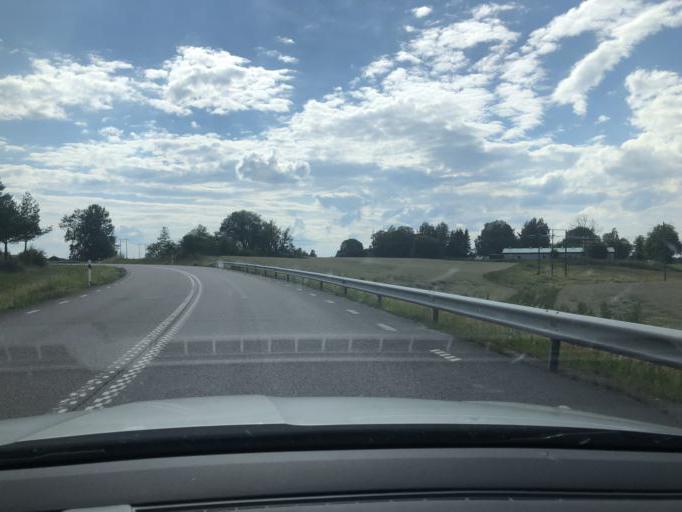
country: SE
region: OEstergoetland
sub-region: Mjolby Kommun
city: Mjolby
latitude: 58.3447
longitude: 15.1740
